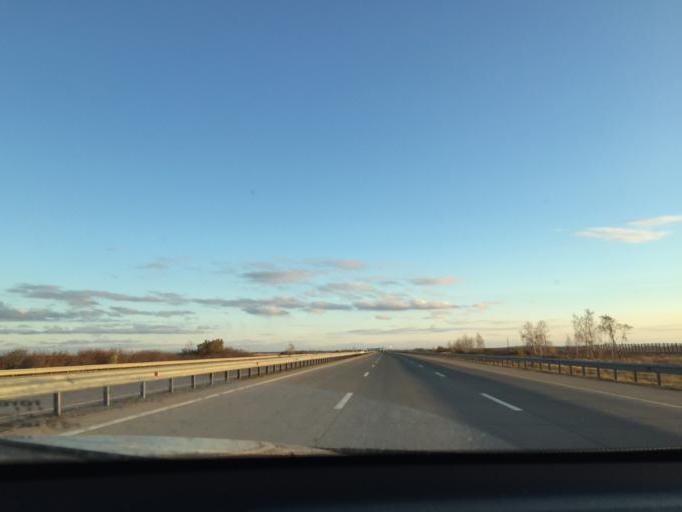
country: KZ
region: Astana Qalasy
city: Astana
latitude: 51.2844
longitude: 71.3617
